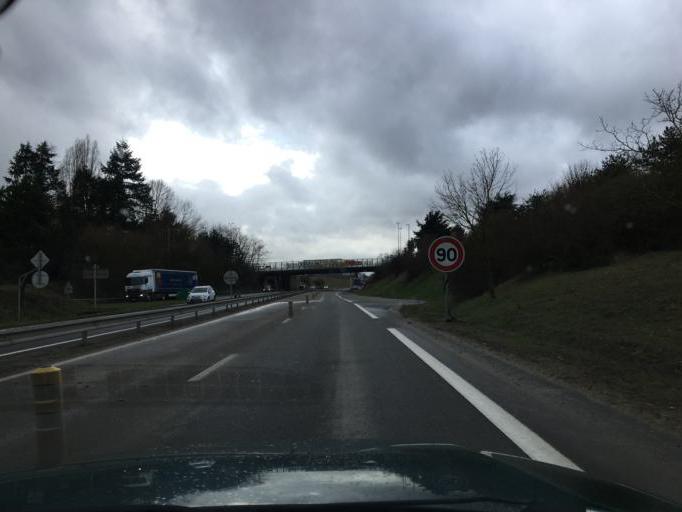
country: FR
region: Centre
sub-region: Departement du Loiret
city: Saran
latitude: 47.9399
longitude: 1.8912
